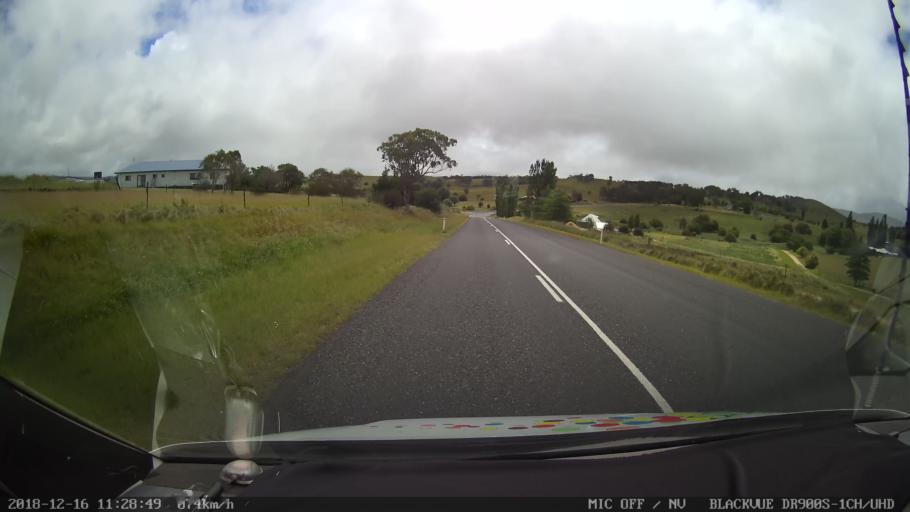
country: AU
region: New South Wales
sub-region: Tenterfield Municipality
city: Carrolls Creek
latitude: -29.0358
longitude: 152.1006
